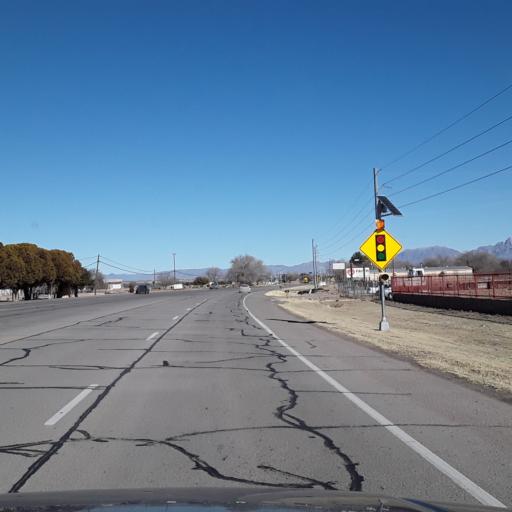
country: US
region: New Mexico
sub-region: Dona Ana County
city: Mesilla
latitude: 32.3006
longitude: -106.8528
